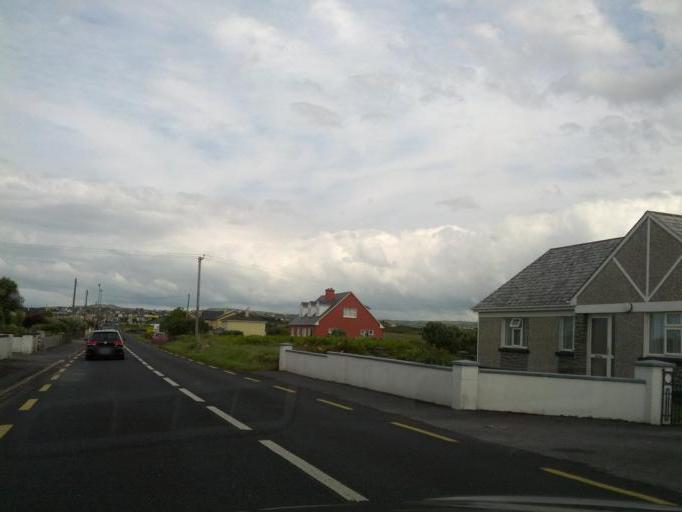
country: IE
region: Munster
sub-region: An Clar
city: Kilrush
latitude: 52.8491
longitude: -9.4138
